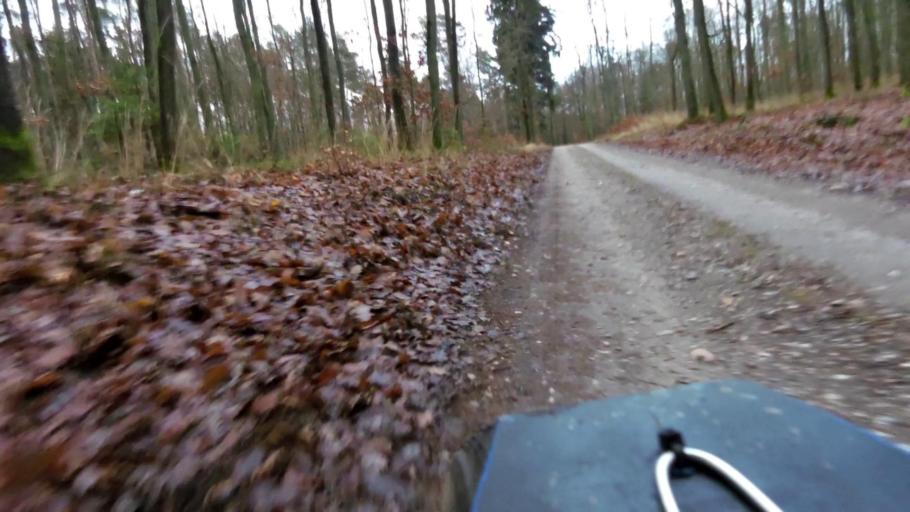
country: PL
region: Lubusz
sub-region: Powiat gorzowski
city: Bogdaniec
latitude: 52.6927
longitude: 15.0060
